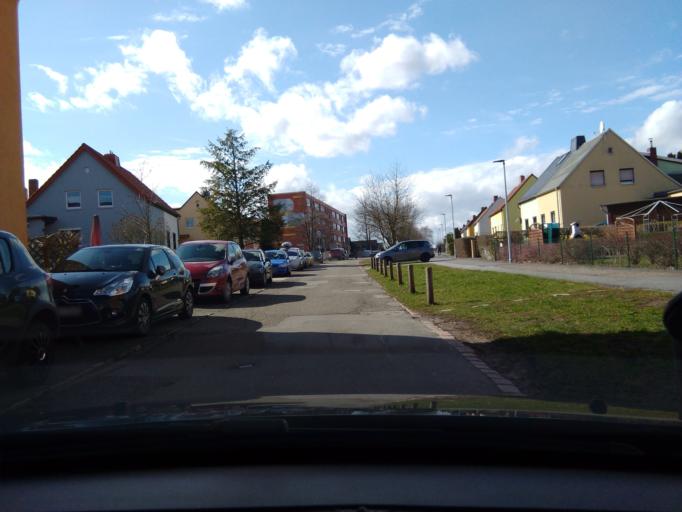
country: DE
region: Saxony
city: Wittgensdorf
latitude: 50.8392
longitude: 12.8753
